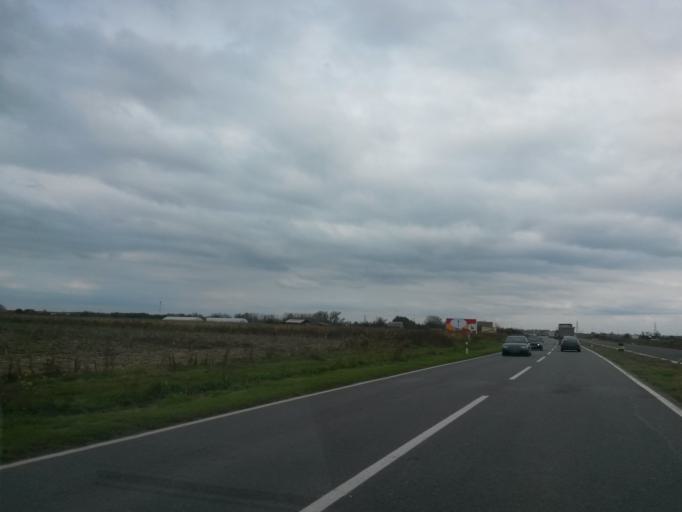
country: HR
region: Osjecko-Baranjska
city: Visnjevac
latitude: 45.5550
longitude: 18.6204
